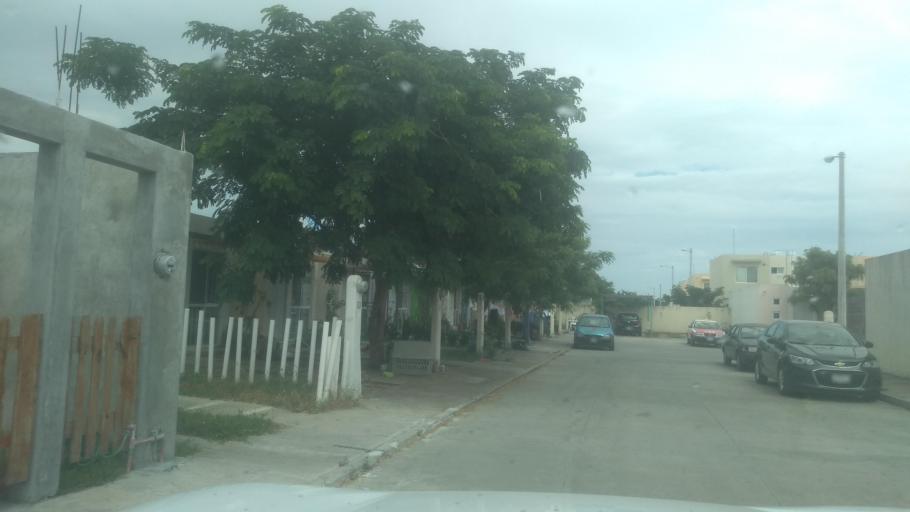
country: MX
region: Veracruz
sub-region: Medellin
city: Fraccionamiento Arboledas San Ramon
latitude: 19.1026
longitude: -96.1688
